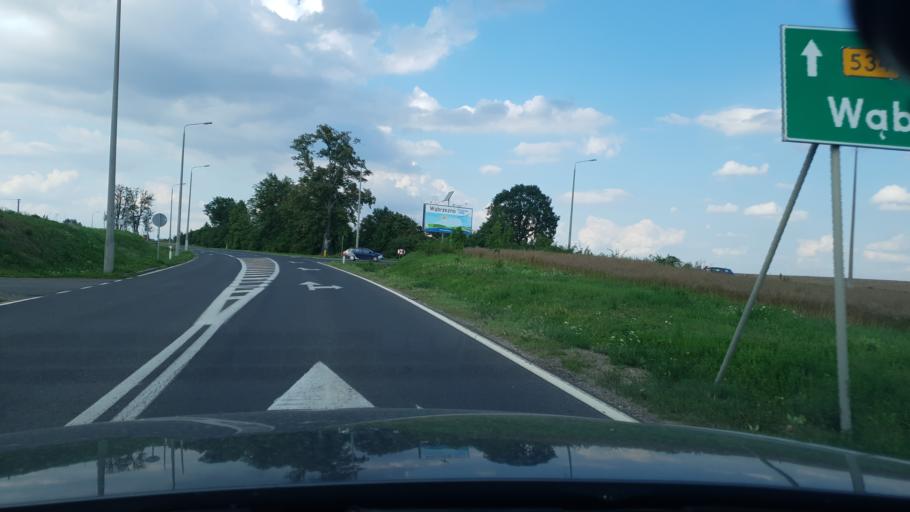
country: PL
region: Kujawsko-Pomorskie
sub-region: Powiat wabrzeski
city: Wabrzezno
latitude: 53.3069
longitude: 18.9341
